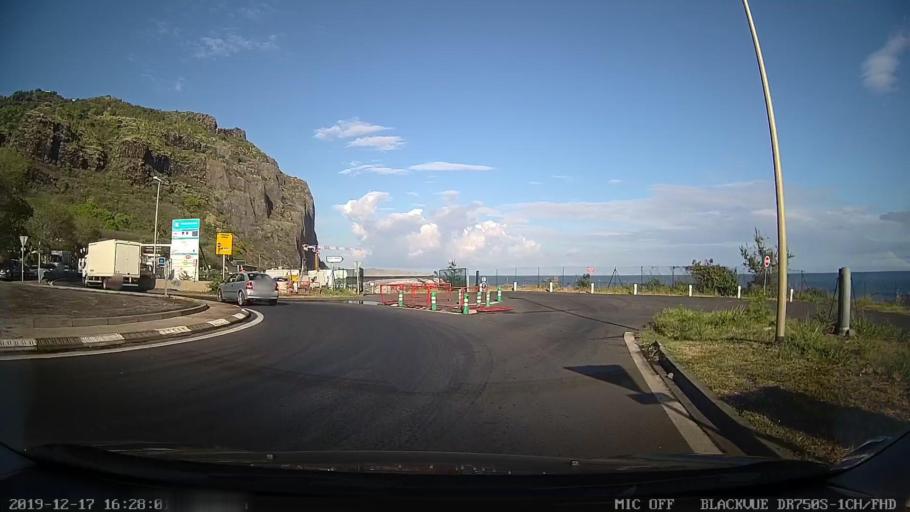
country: RE
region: Reunion
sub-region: Reunion
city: Saint-Denis
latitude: -20.8775
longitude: 55.4410
